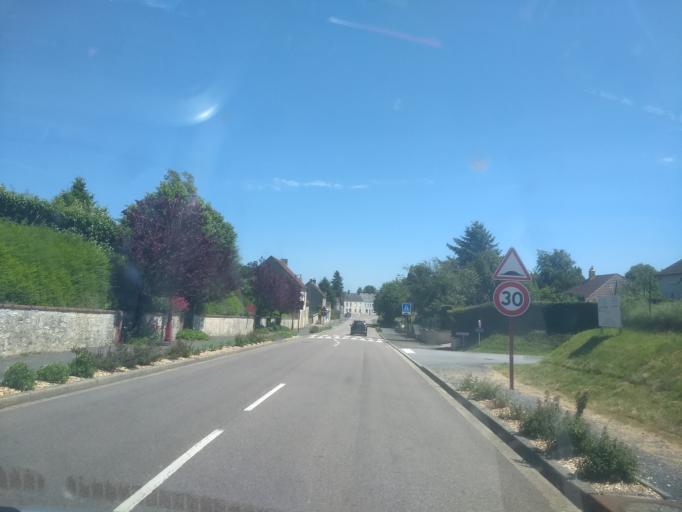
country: FR
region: Lower Normandy
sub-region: Departement de l'Orne
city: Belleme
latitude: 48.4087
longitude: 0.6543
